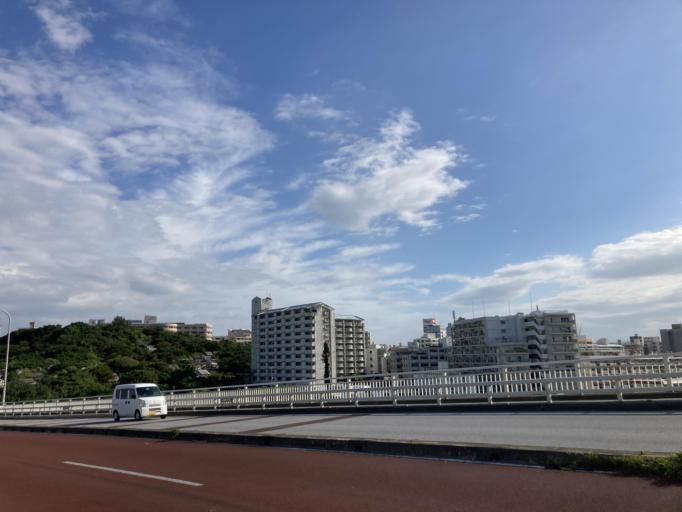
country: JP
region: Okinawa
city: Naha-shi
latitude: 26.2277
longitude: 127.6812
